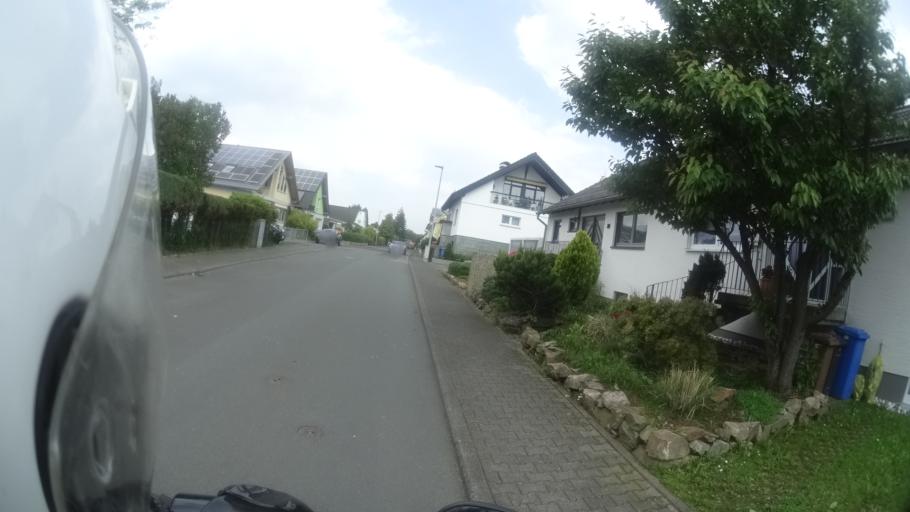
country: DE
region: Hesse
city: Taunusstein
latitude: 50.1294
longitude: 8.1453
